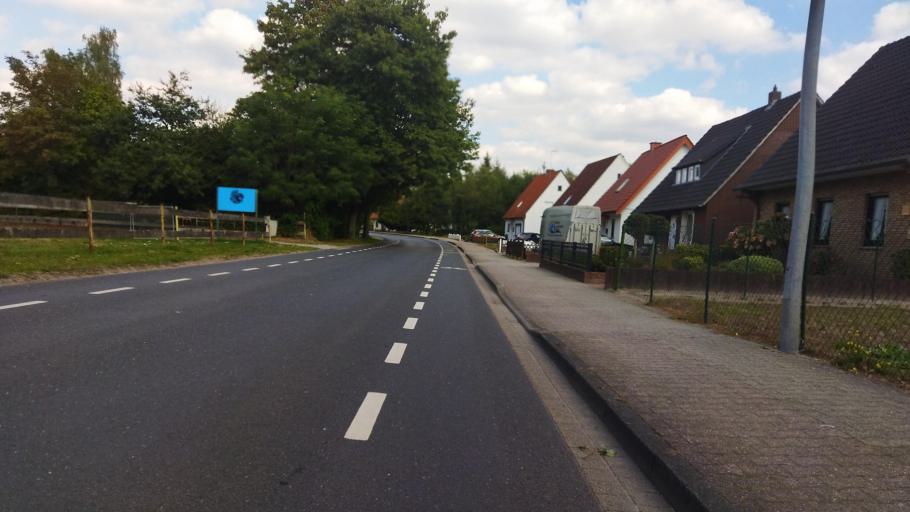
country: DE
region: Lower Saxony
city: Haren
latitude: 52.7939
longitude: 7.2661
